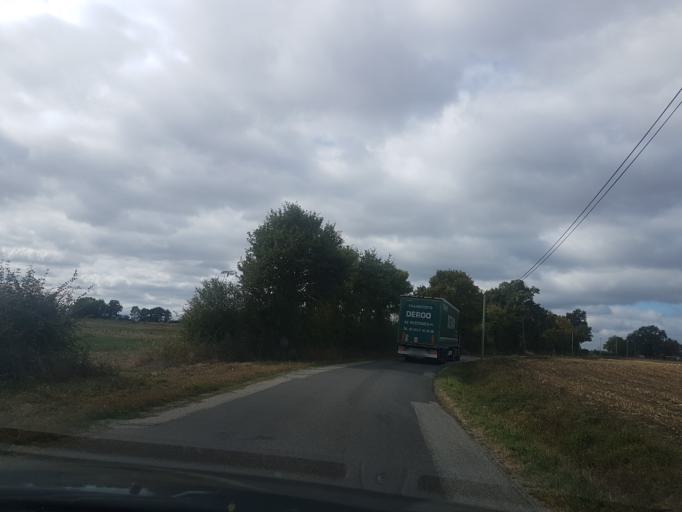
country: FR
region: Pays de la Loire
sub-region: Departement de la Loire-Atlantique
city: Ligne
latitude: 47.3986
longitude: -1.3971
